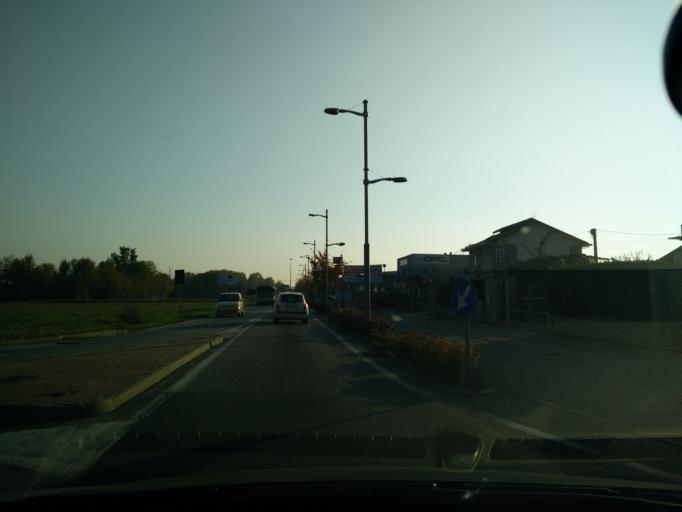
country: IT
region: Piedmont
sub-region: Provincia di Torino
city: Leini
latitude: 45.1429
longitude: 7.7065
